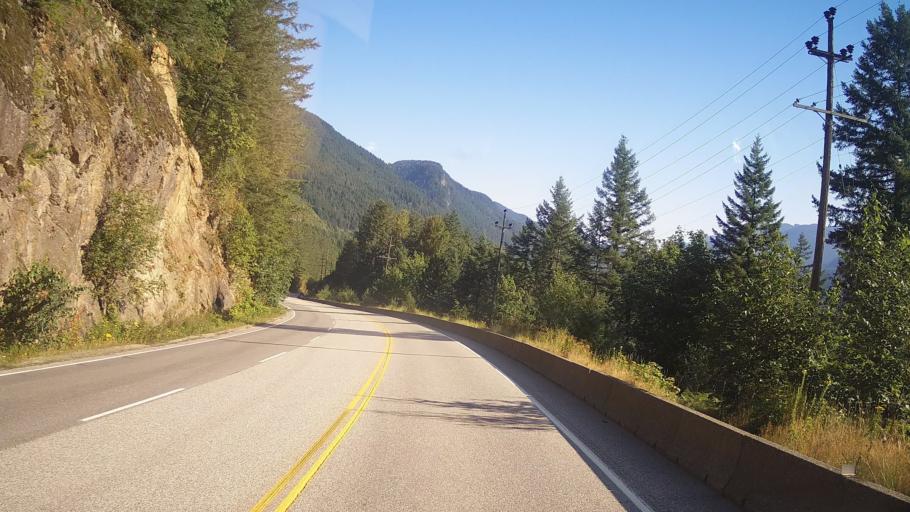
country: CA
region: British Columbia
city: Hope
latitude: 49.4202
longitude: -121.4368
